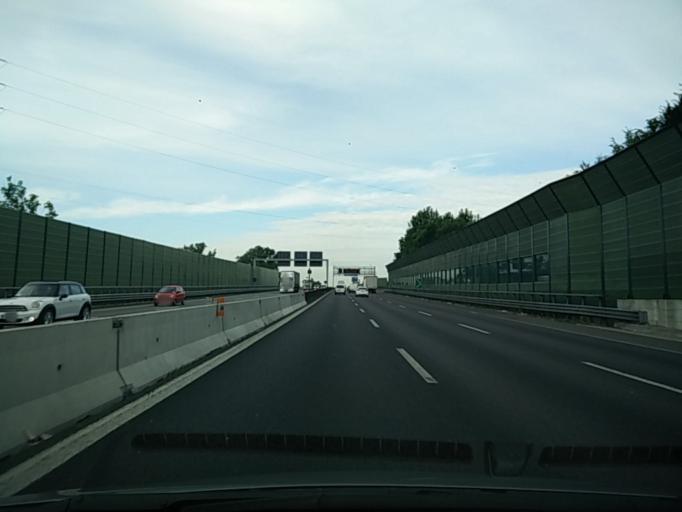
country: IT
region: Lombardy
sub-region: Provincia di Monza e Brianza
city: Monza
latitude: 45.5545
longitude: 9.2574
